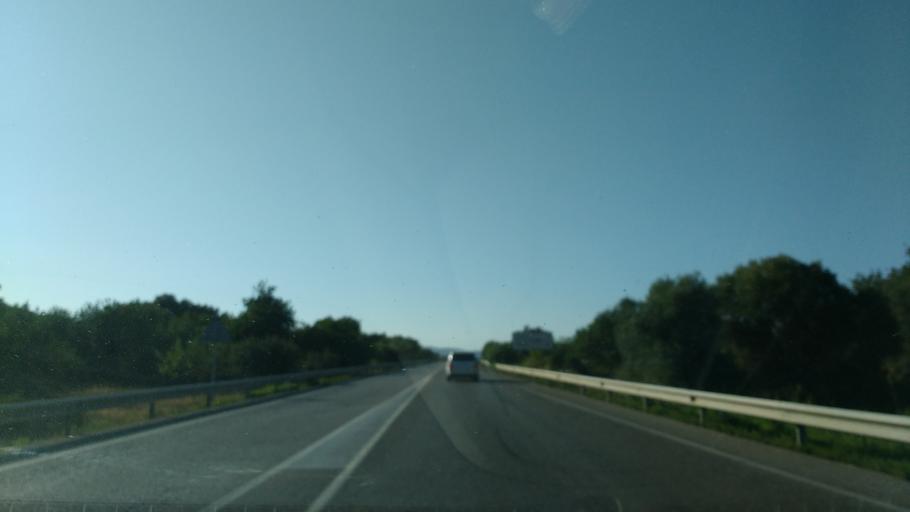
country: ES
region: Balearic Islands
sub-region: Illes Balears
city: Alcudia
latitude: 39.8378
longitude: 3.1012
